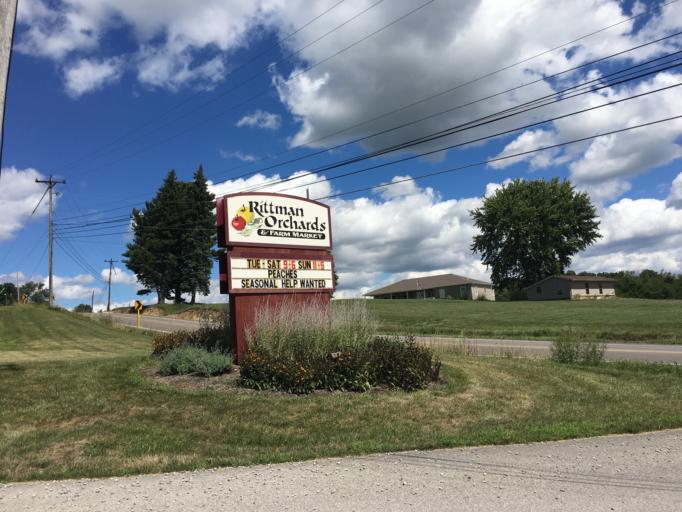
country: US
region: Ohio
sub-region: Wayne County
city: Doylestown
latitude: 40.9644
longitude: -81.7385
